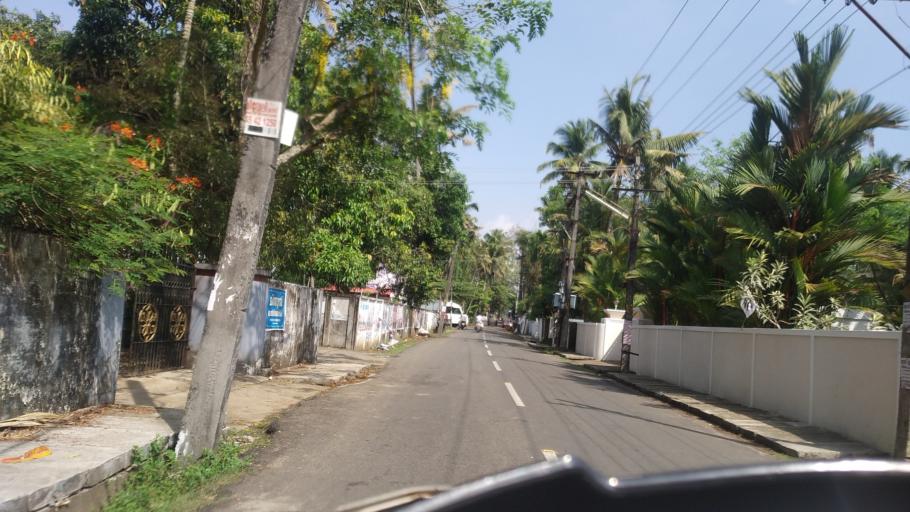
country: IN
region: Kerala
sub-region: Thrissur District
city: Kodungallur
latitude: 10.1338
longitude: 76.2212
